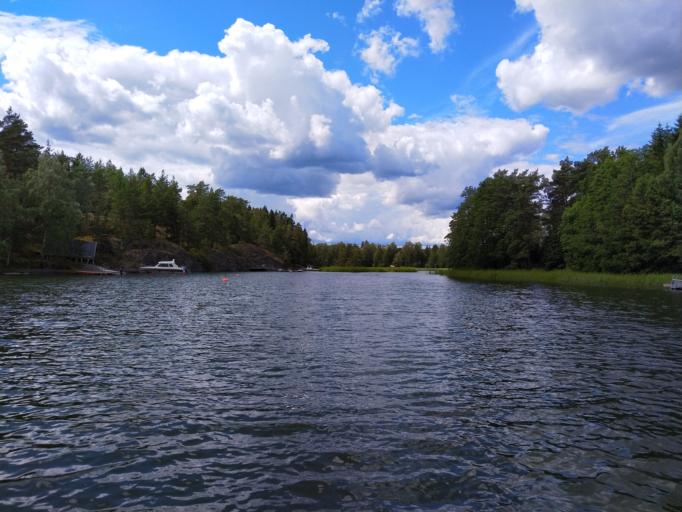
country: FI
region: Uusimaa
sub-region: Raaseporin
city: Karis
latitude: 59.9711
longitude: 23.7101
